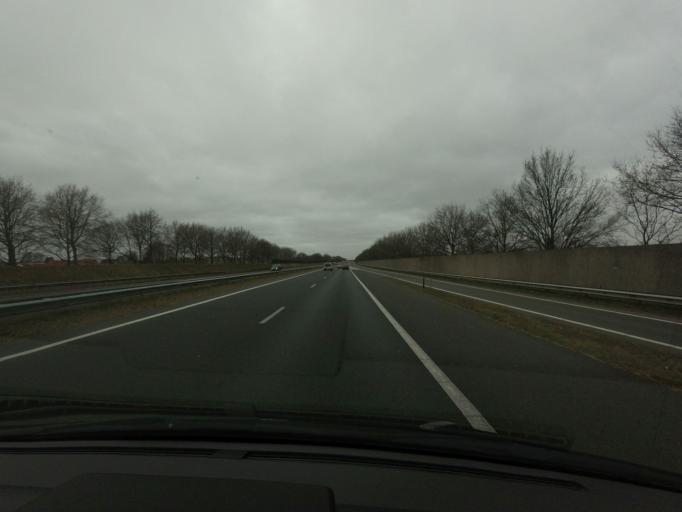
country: NL
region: Groningen
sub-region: Gemeente Hoogezand-Sappemeer
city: Sappemeer
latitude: 53.1680
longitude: 6.8018
